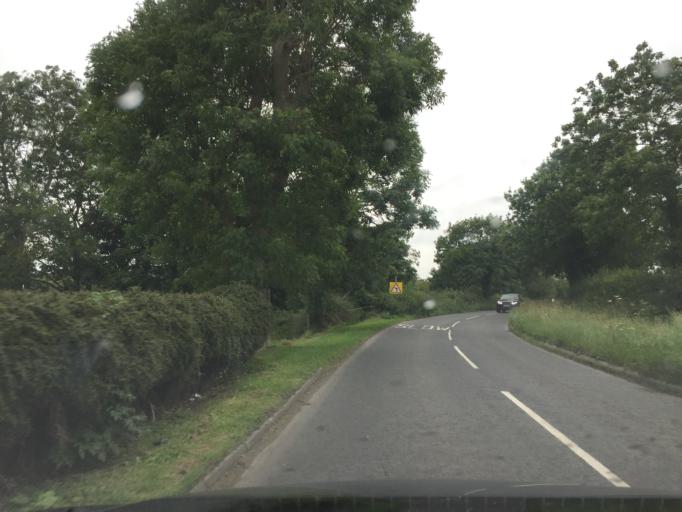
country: GB
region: Northern Ireland
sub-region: Down District
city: Kircubbin
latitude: 54.4926
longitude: -5.4992
